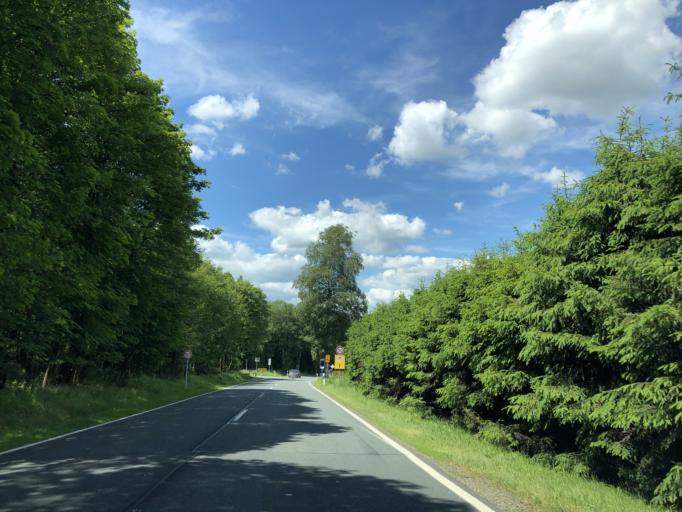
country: DE
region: North Rhine-Westphalia
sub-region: Regierungsbezirk Arnsberg
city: Erndtebruck
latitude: 50.9877
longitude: 8.3124
